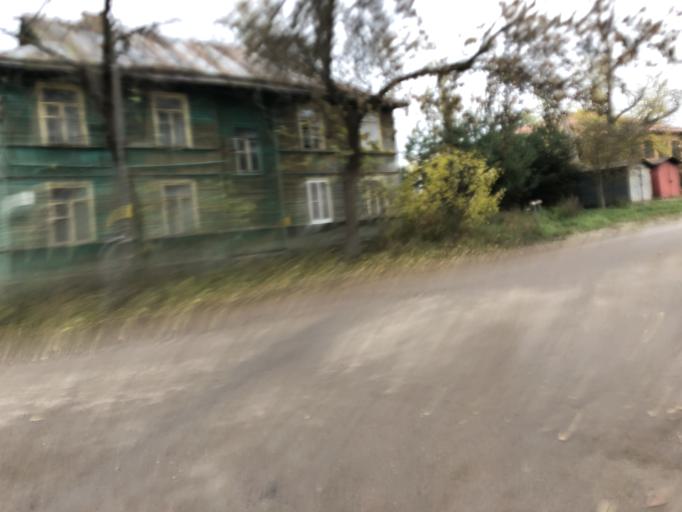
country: RU
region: Tverskaya
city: Rzhev
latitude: 56.2586
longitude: 34.3248
